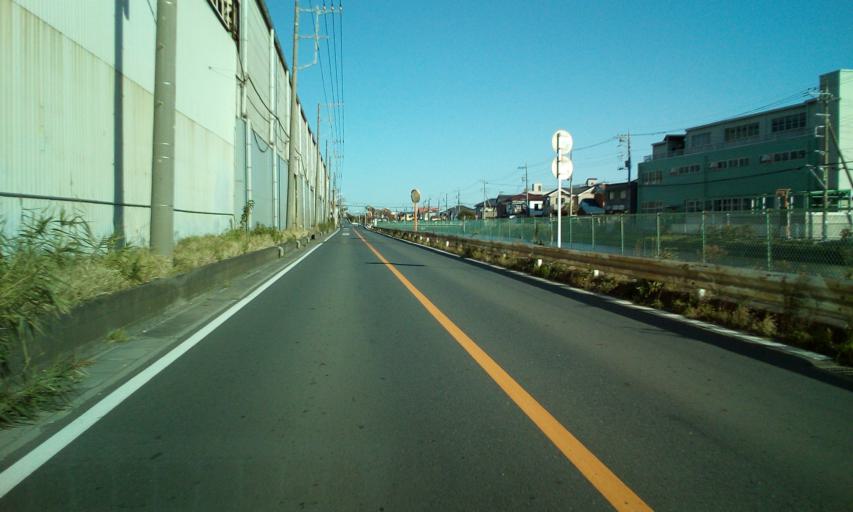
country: JP
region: Chiba
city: Matsudo
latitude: 35.8135
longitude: 139.8837
